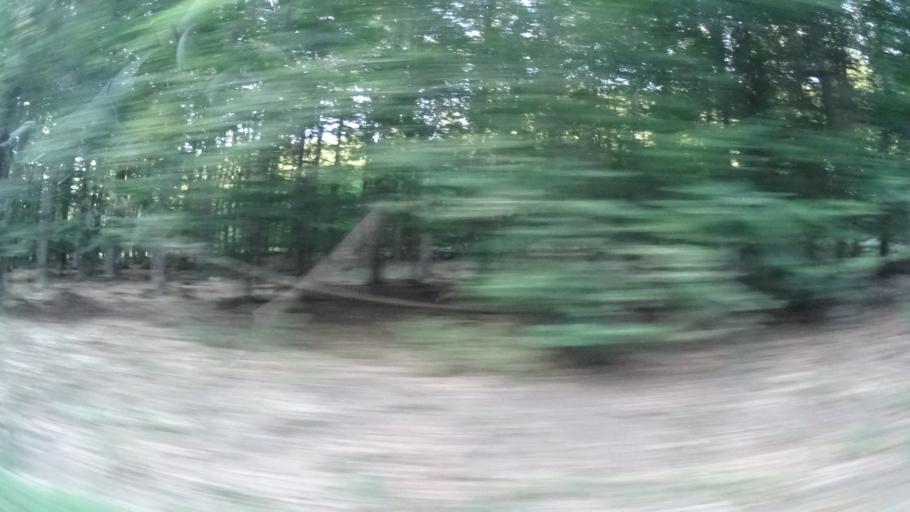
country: DE
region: Hesse
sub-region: Regierungsbezirk Darmstadt
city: Gelnhausen
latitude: 50.2570
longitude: 9.1985
